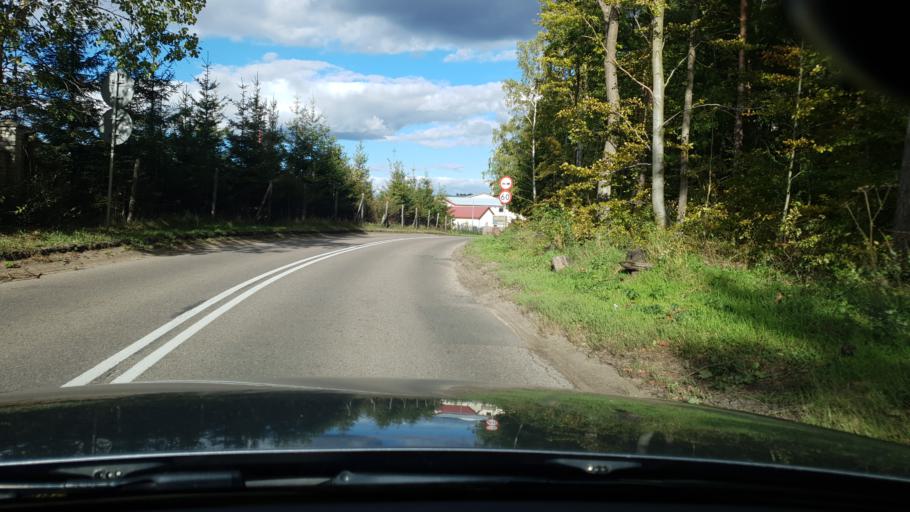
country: PL
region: Pomeranian Voivodeship
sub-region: Powiat wejherowski
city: Bojano
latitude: 54.5080
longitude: 18.3810
